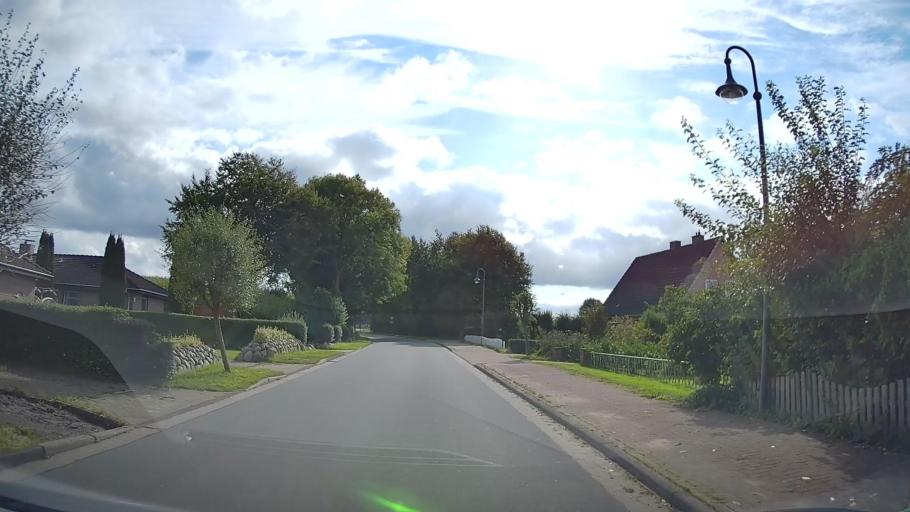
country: DE
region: Schleswig-Holstein
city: Ringsberg
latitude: 54.8052
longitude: 9.5983
